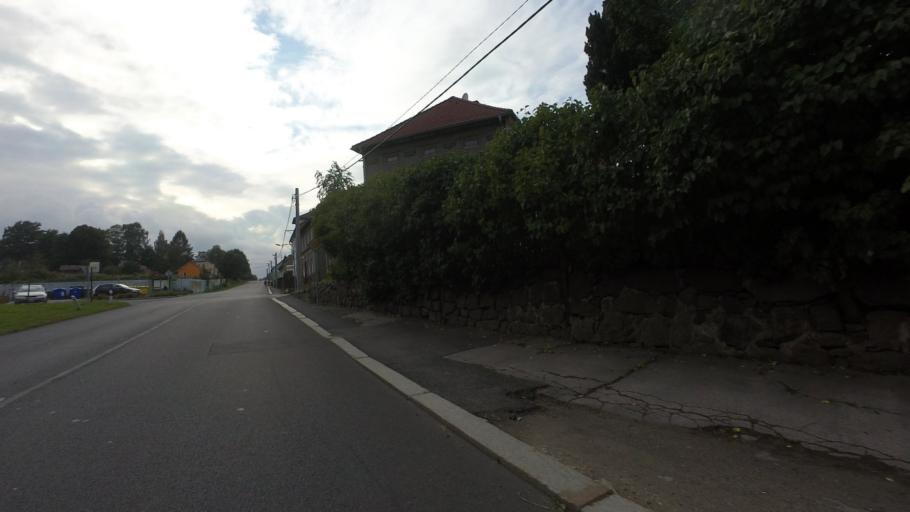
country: CZ
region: Ustecky
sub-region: Okres Decin
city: Sluknov
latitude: 51.0023
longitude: 14.4446
